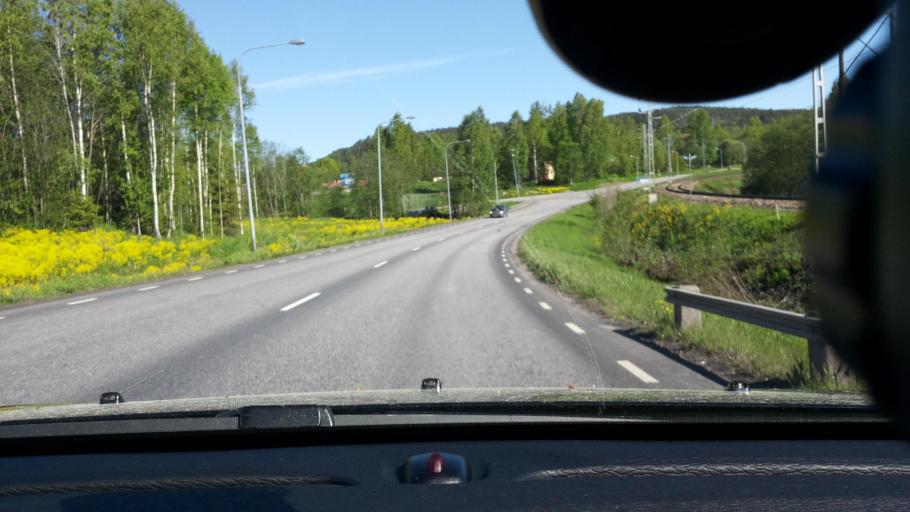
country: SE
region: Vaesternorrland
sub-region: Timra Kommun
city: Timra
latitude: 62.4709
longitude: 17.3155
